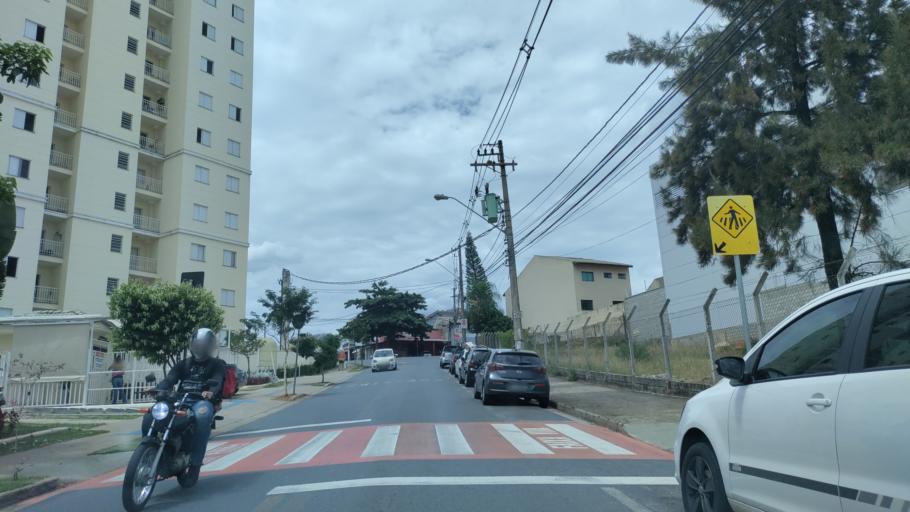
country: BR
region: Sao Paulo
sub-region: Sorocaba
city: Sorocaba
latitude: -23.4786
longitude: -47.4543
